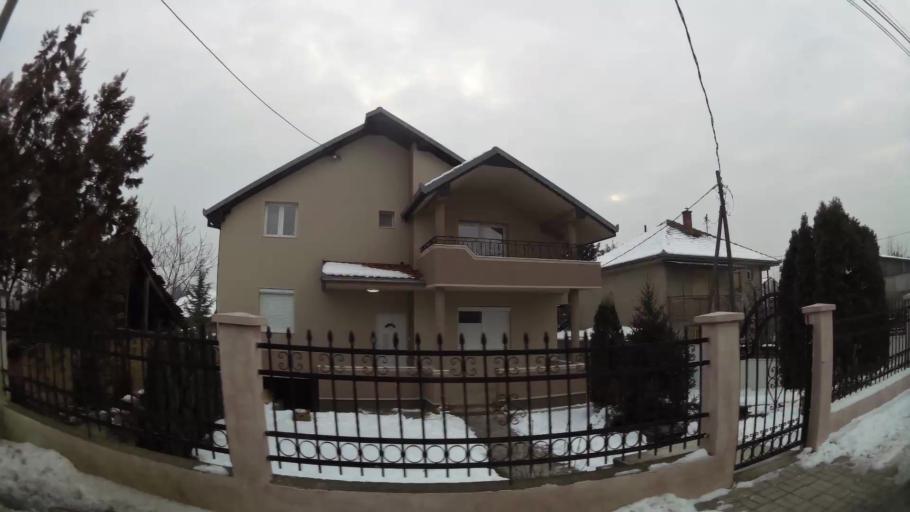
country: MK
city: Kondovo
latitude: 42.0454
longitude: 21.3505
